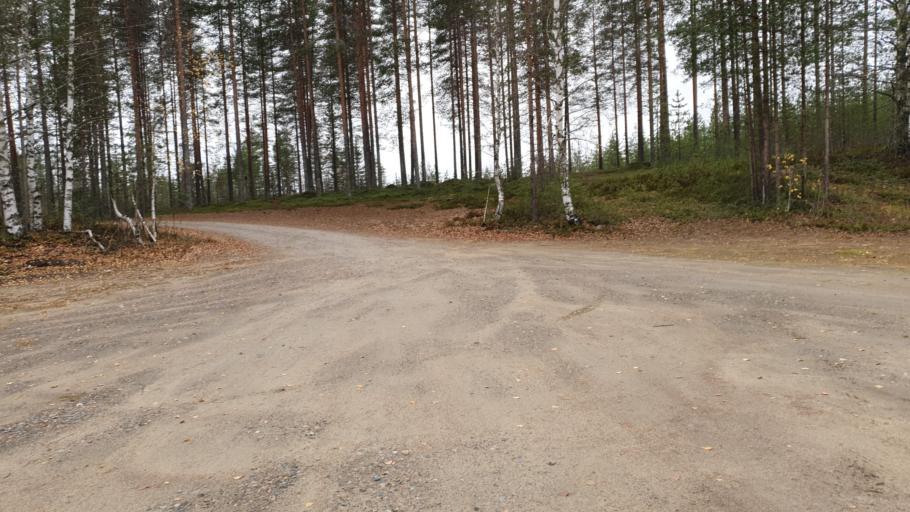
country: FI
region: Kainuu
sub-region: Kehys-Kainuu
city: Kuhmo
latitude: 64.1490
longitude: 29.4032
